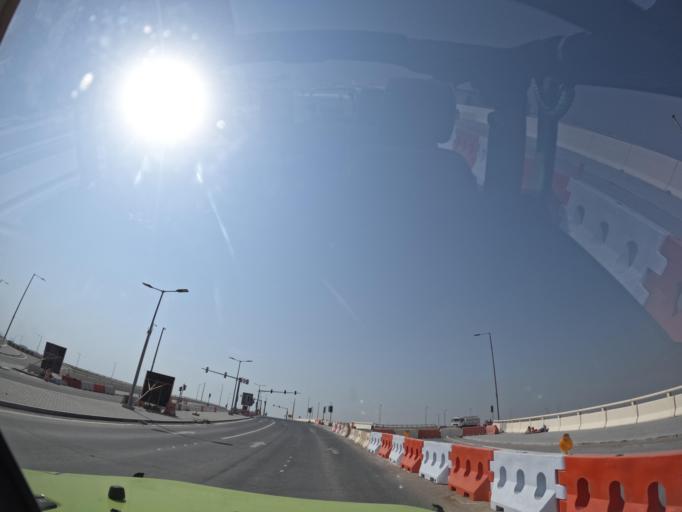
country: AE
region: Abu Dhabi
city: Abu Dhabi
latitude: 24.4640
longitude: 54.6302
